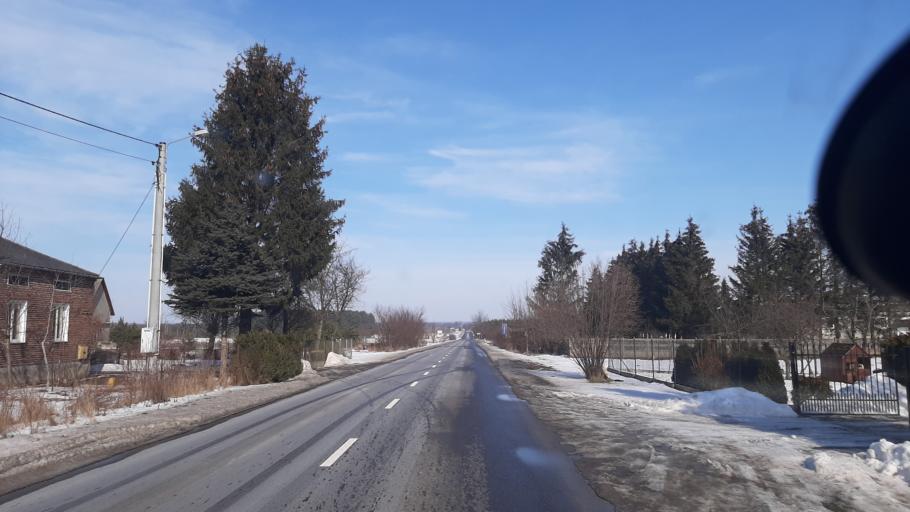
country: PL
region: Lublin Voivodeship
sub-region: Powiat pulawski
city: Kurow
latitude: 51.3980
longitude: 22.1989
